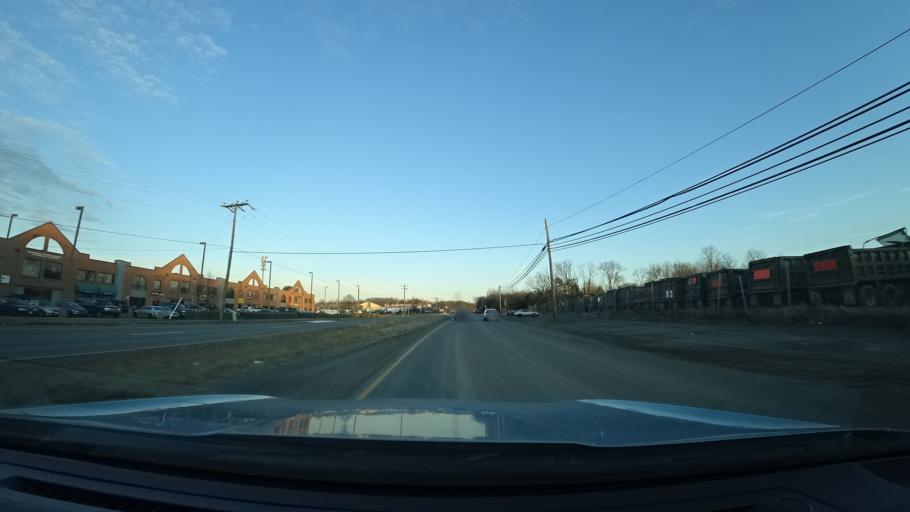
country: US
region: Virginia
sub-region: Loudoun County
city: Oak Grove
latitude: 38.9782
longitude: -77.4167
